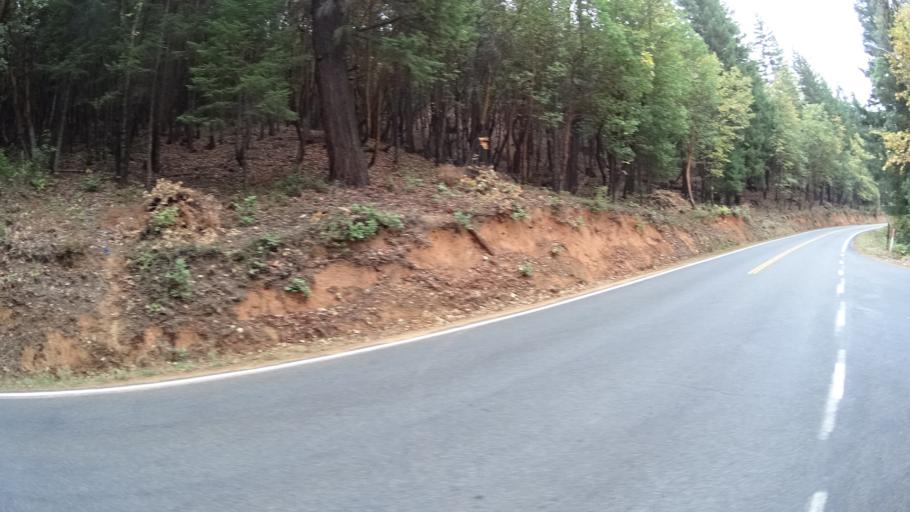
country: US
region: California
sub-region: Siskiyou County
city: Happy Camp
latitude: 41.8084
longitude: -123.3794
